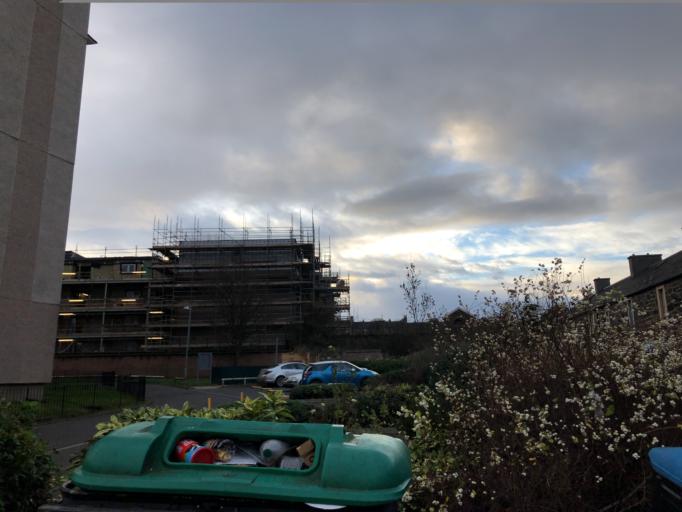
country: GB
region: Scotland
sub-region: Edinburgh
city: Edinburgh
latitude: 55.9636
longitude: -3.1799
